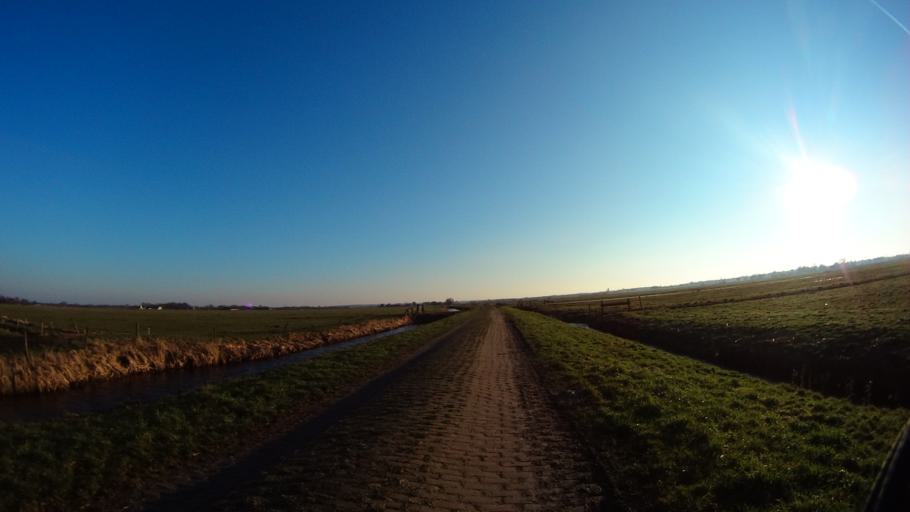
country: NL
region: Utrecht
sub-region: Gemeente Baarn
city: Baarn
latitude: 52.1991
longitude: 5.3214
